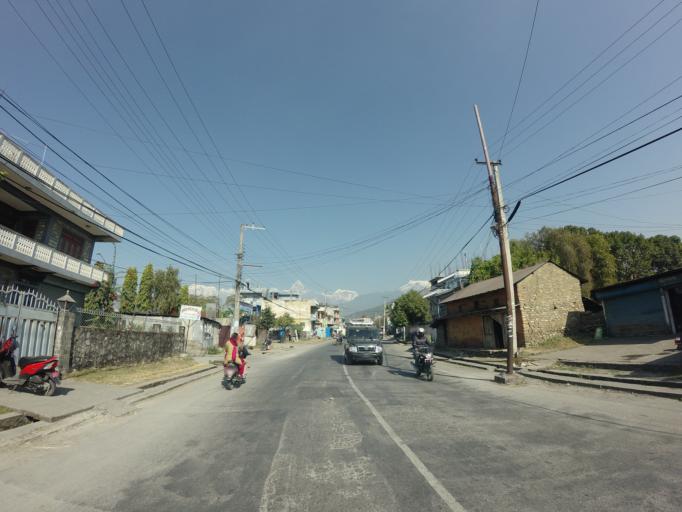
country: NP
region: Western Region
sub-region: Gandaki Zone
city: Pokhara
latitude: 28.2182
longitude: 83.9976
